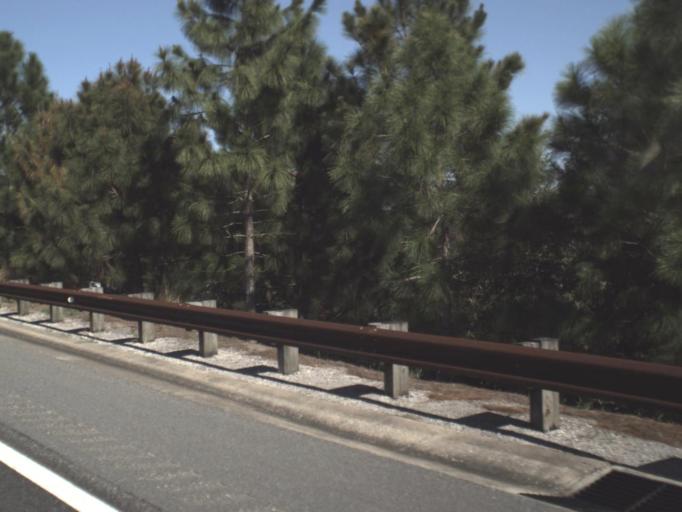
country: US
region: Florida
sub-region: Pasco County
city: Odessa
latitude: 28.1886
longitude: -82.5433
